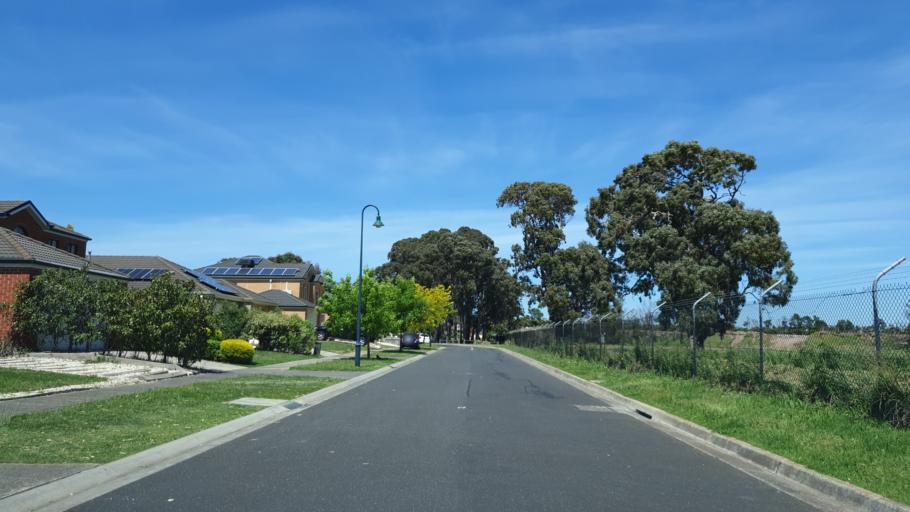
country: AU
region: Victoria
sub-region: Casey
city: Cranbourne North
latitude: -38.0643
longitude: 145.2806
